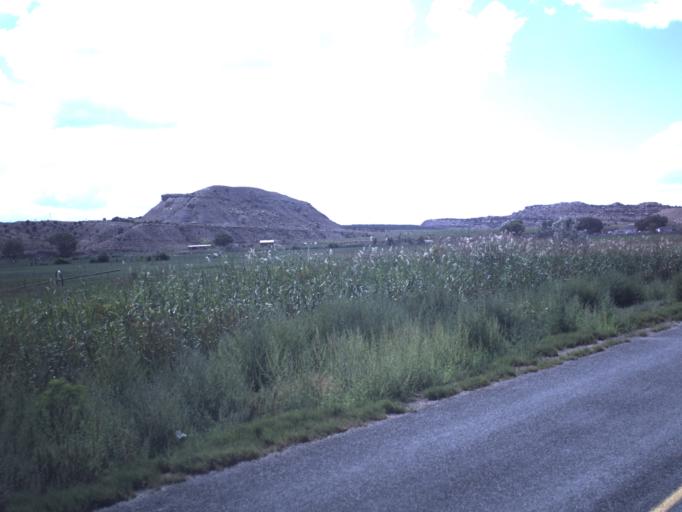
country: US
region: Utah
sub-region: Duchesne County
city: Duchesne
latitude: 40.1720
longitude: -110.4231
